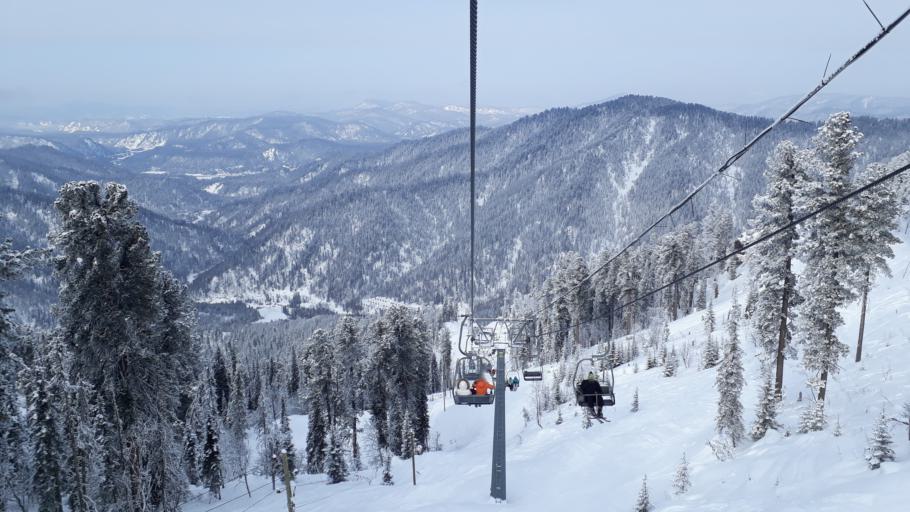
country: RU
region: Altay
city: Iogach
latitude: 51.7320
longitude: 87.2997
